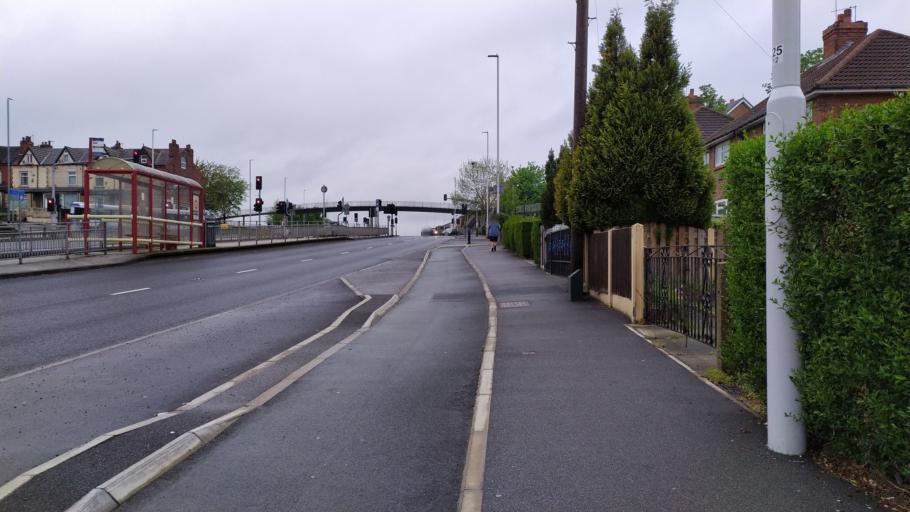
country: GB
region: England
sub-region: City and Borough of Leeds
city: Chapel Allerton
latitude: 53.8017
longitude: -1.4966
